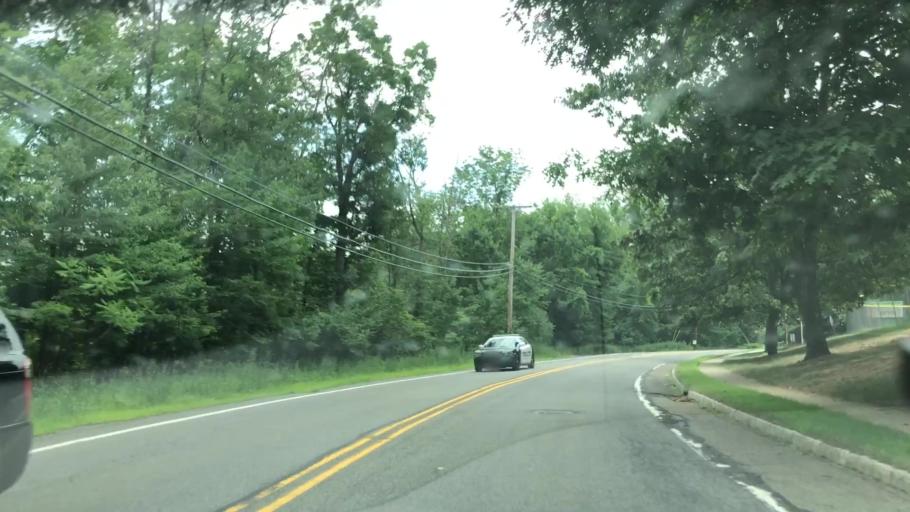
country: US
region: New Jersey
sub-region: Morris County
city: Mount Arlington
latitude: 40.9178
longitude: -74.6366
